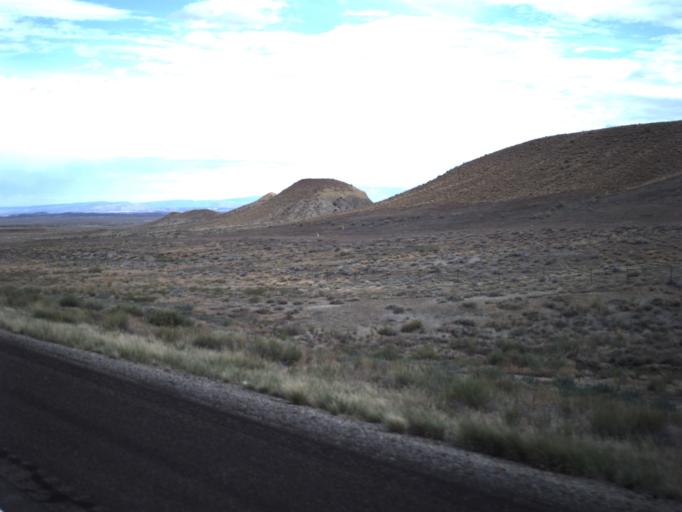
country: US
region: Utah
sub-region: Grand County
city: Moab
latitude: 38.9484
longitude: -109.6701
